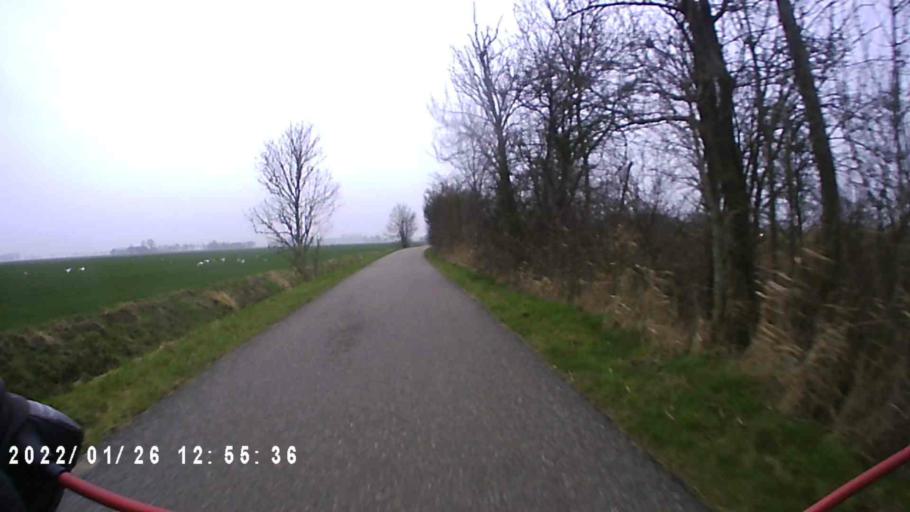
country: NL
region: Groningen
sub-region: Gemeente Winsum
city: Winsum
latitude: 53.3456
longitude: 6.4817
